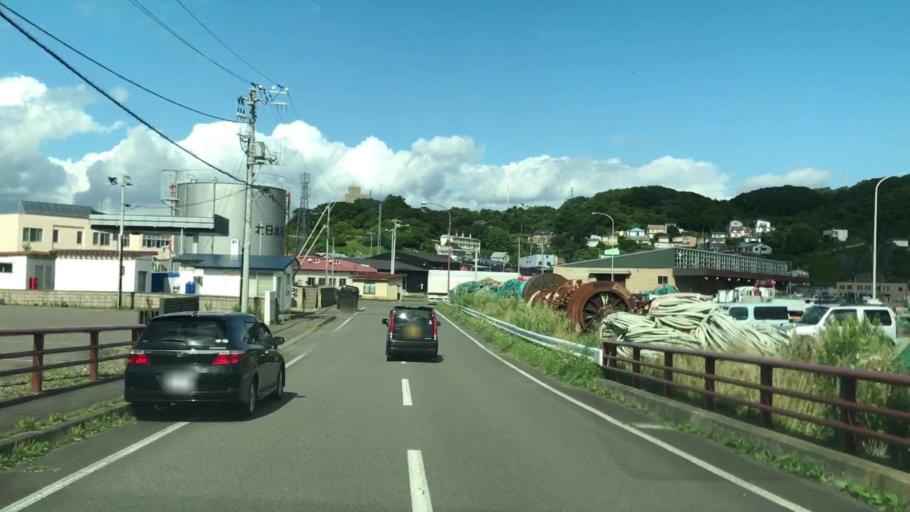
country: JP
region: Hokkaido
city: Muroran
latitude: 42.3082
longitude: 140.9704
